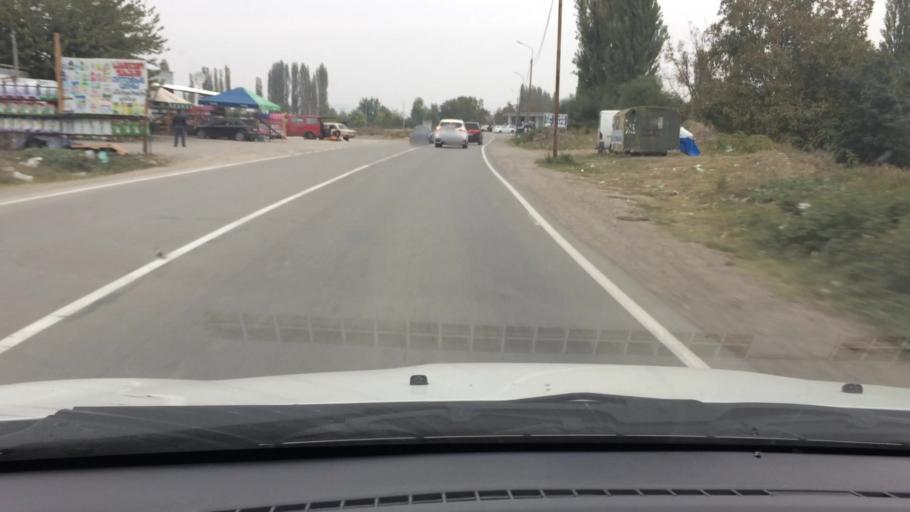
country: AM
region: Tavush
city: Bagratashen
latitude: 41.2526
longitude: 44.7996
